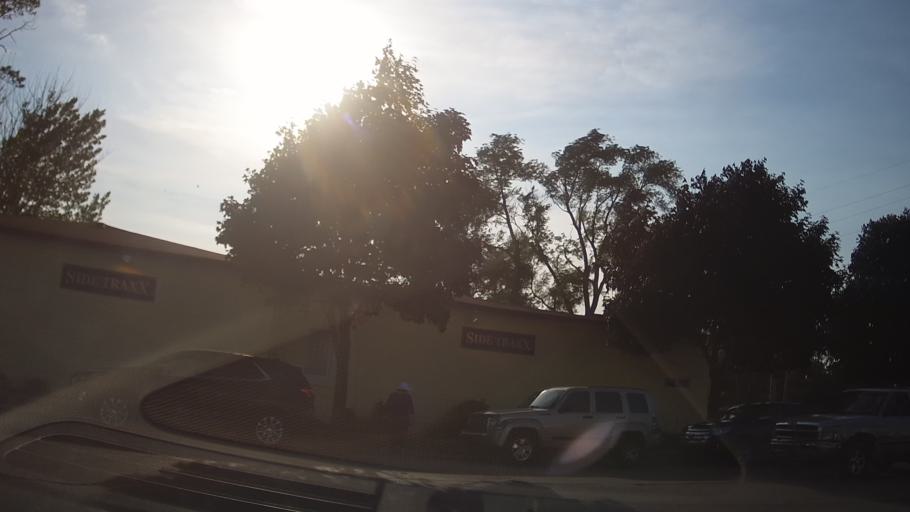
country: US
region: Michigan
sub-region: Grand Traverse County
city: Traverse City
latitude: 44.7584
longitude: -85.6110
